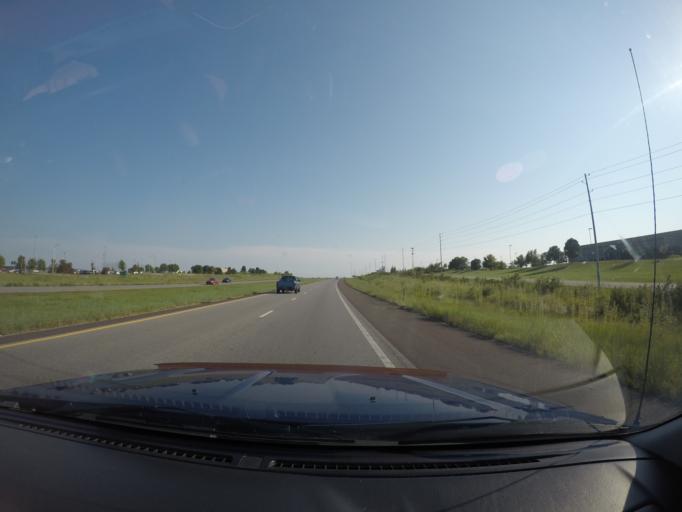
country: US
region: Kansas
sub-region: Wyandotte County
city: Bonner Springs
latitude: 38.9853
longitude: -94.8533
